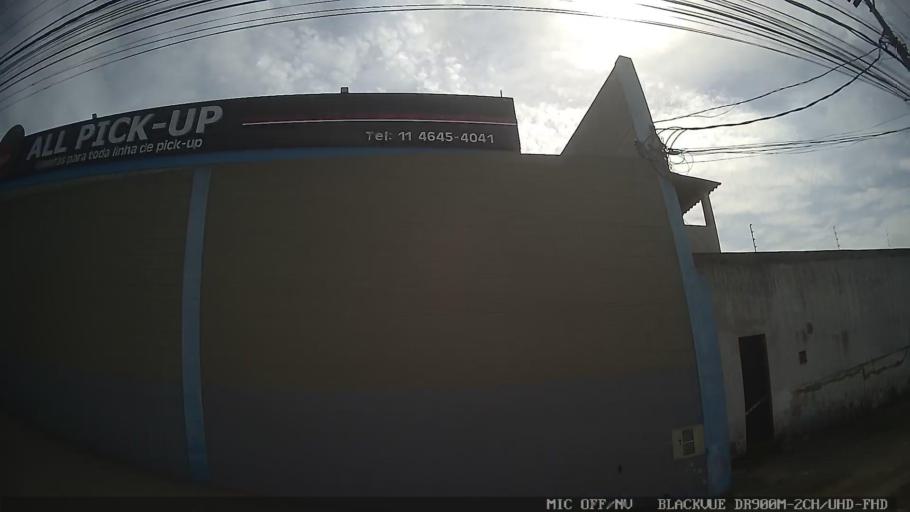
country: BR
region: Sao Paulo
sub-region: Itaquaquecetuba
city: Itaquaquecetuba
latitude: -23.4780
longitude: -46.3216
